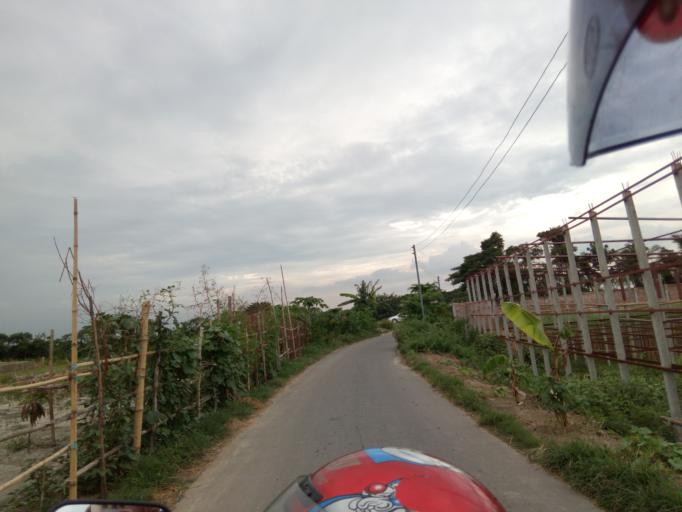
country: BD
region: Dhaka
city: Paltan
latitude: 23.7461
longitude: 90.4748
